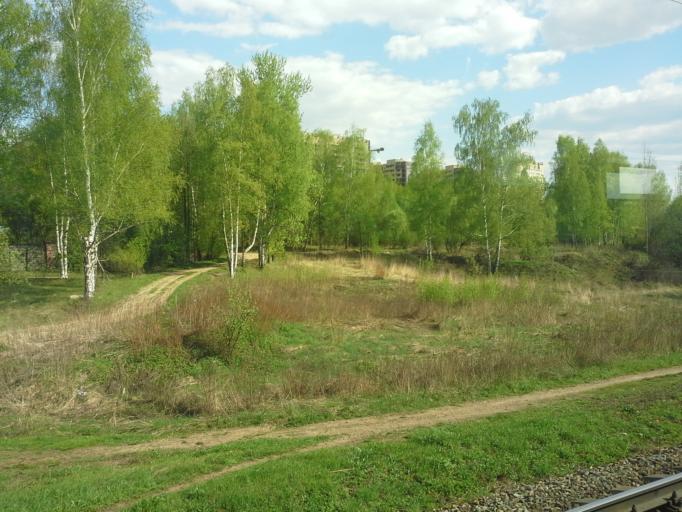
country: RU
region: Moskovskaya
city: Pushkino
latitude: 56.0304
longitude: 37.8492
